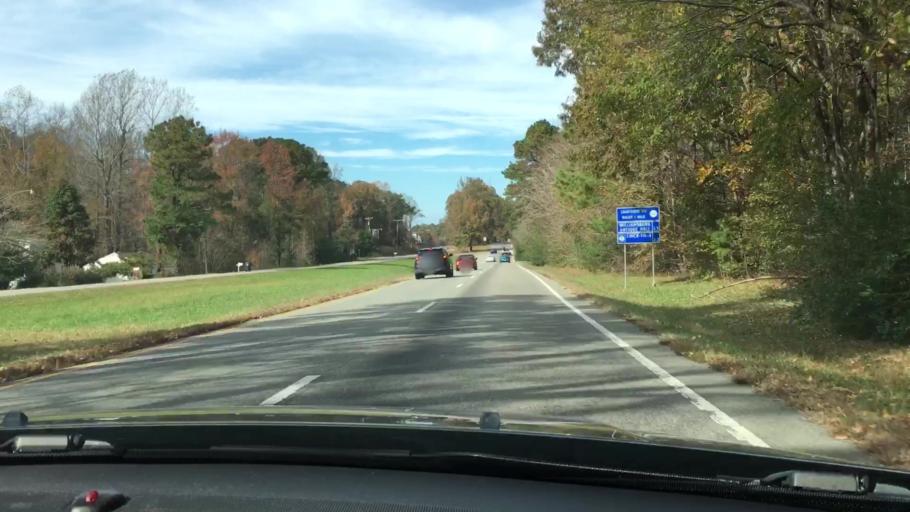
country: US
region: Virginia
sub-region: James City County
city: Williamsburg
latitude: 37.3300
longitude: -76.7427
